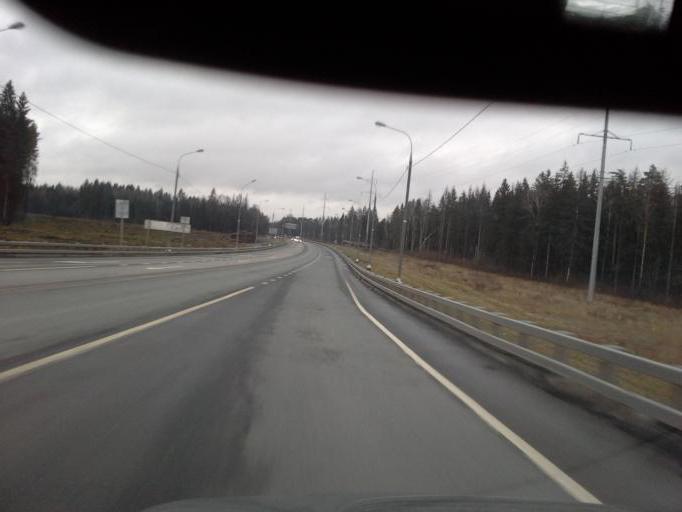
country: RU
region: Moskovskaya
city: Zhavoronki
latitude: 55.6196
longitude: 37.0985
